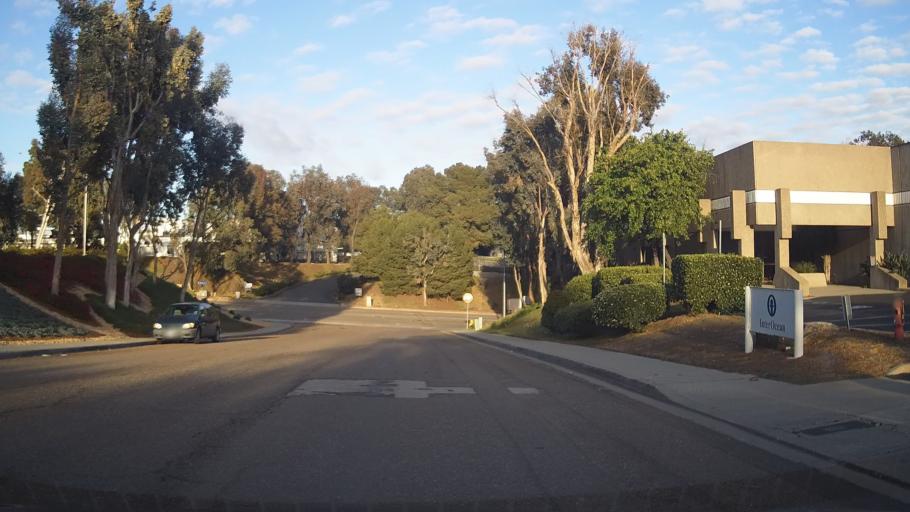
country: US
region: California
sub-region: San Diego County
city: San Diego
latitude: 32.8119
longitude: -117.1211
